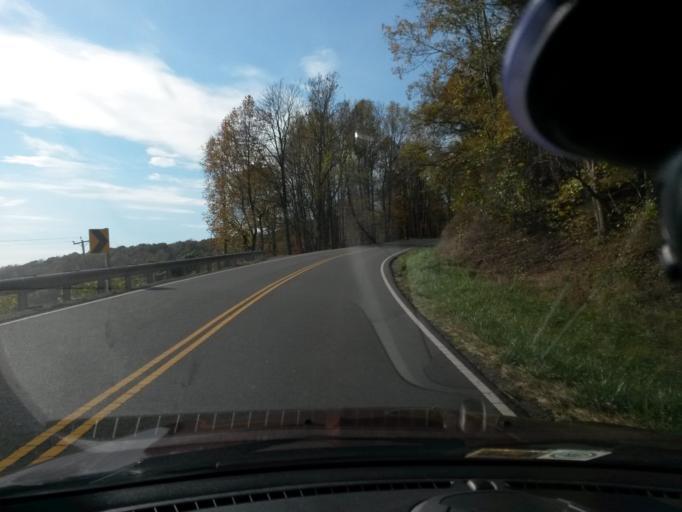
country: US
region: Virginia
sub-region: Franklin County
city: North Shore
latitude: 37.1226
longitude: -79.7833
